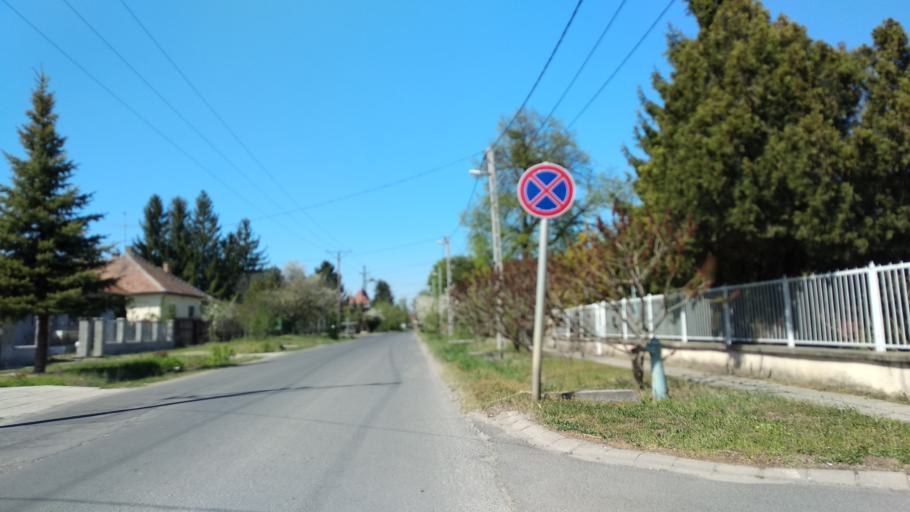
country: HU
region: Pest
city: Godollo
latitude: 47.5870
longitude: 19.3536
